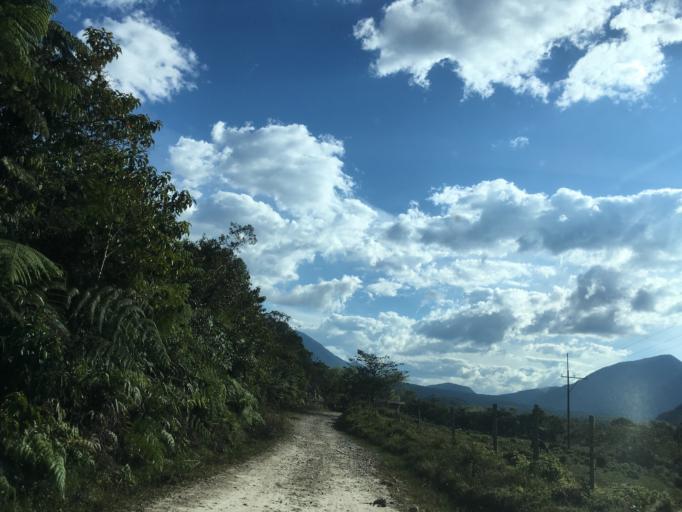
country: CO
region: Santander
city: Oiba
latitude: 6.0938
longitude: -73.1985
